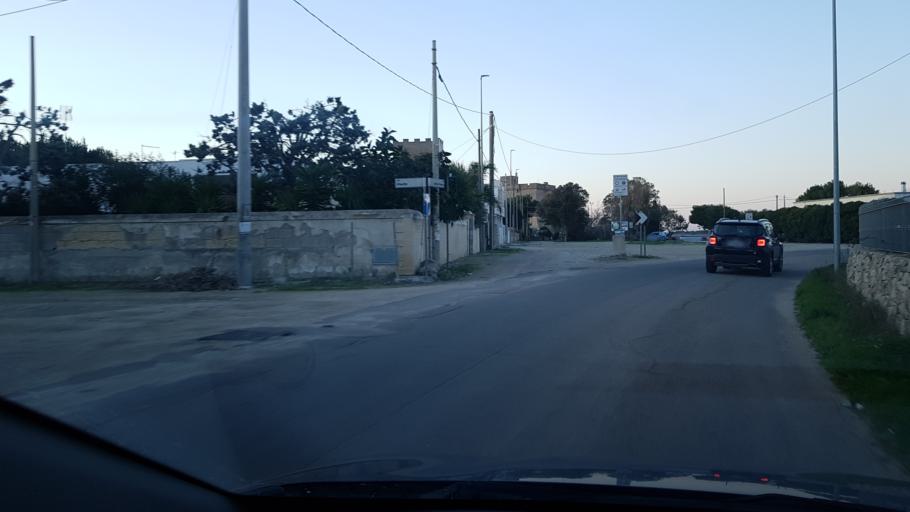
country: IT
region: Apulia
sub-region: Provincia di Lecce
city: Porto Cesareo
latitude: 40.2153
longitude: 17.9235
